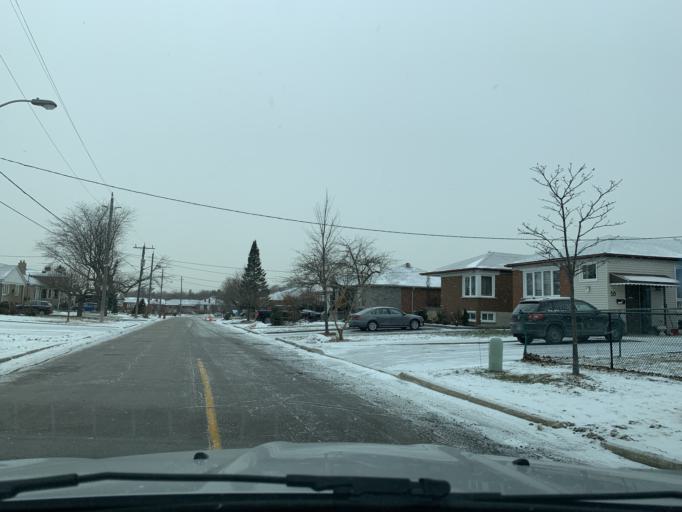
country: CA
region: Ontario
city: Concord
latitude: 43.7366
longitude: -79.4871
